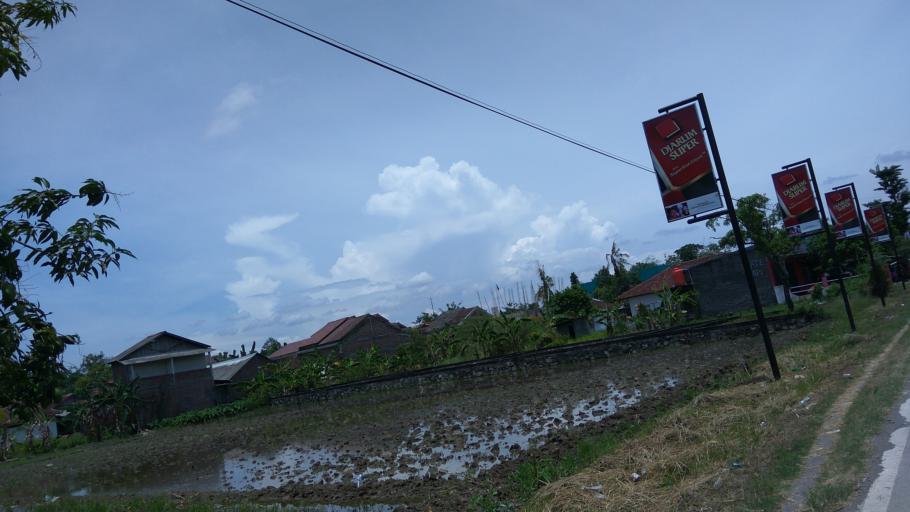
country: ID
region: Central Java
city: Mranggen
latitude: -7.0497
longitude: 110.6007
